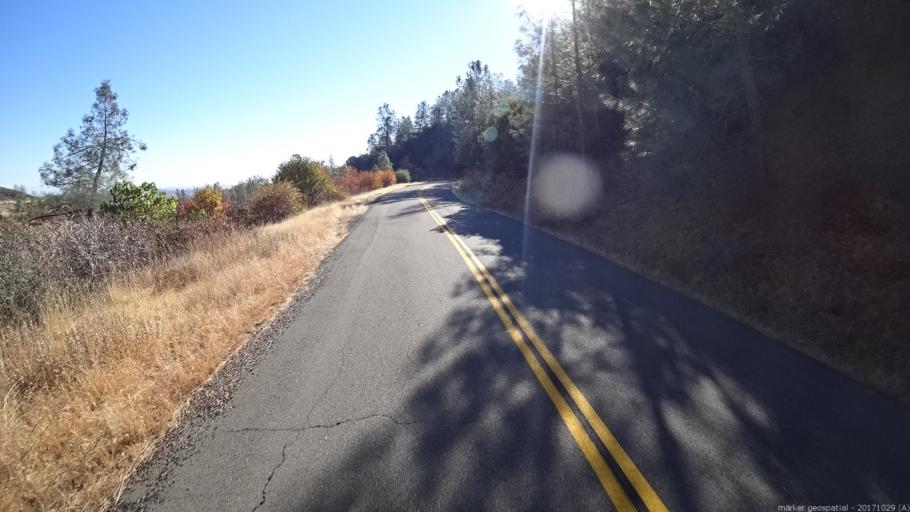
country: US
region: California
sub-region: Trinity County
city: Lewiston
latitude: 40.3795
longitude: -122.8470
